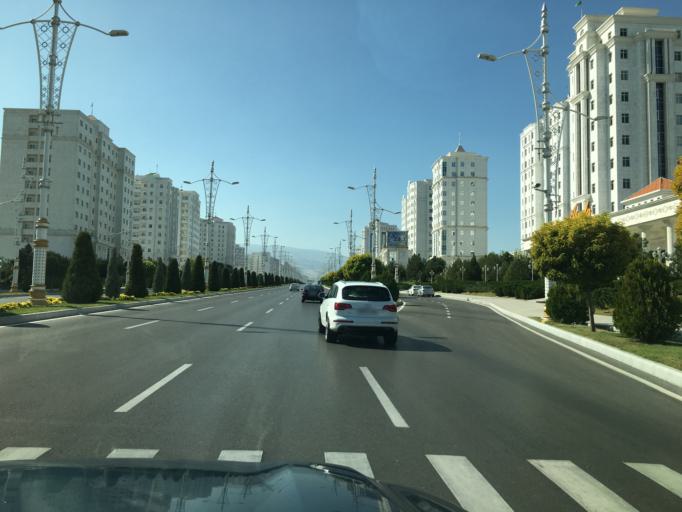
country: TM
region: Ahal
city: Ashgabat
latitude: 37.9258
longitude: 58.3702
